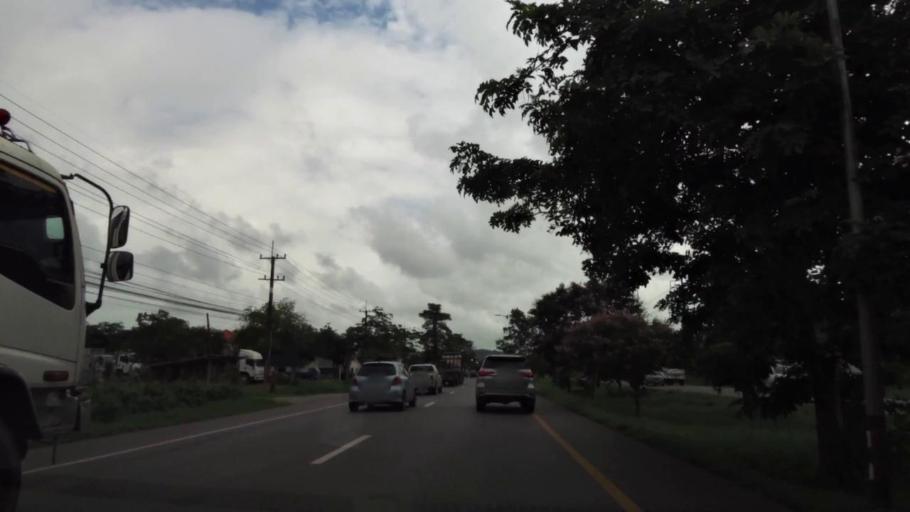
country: TH
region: Chanthaburi
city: Na Yai Am
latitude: 12.7324
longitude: 101.9074
